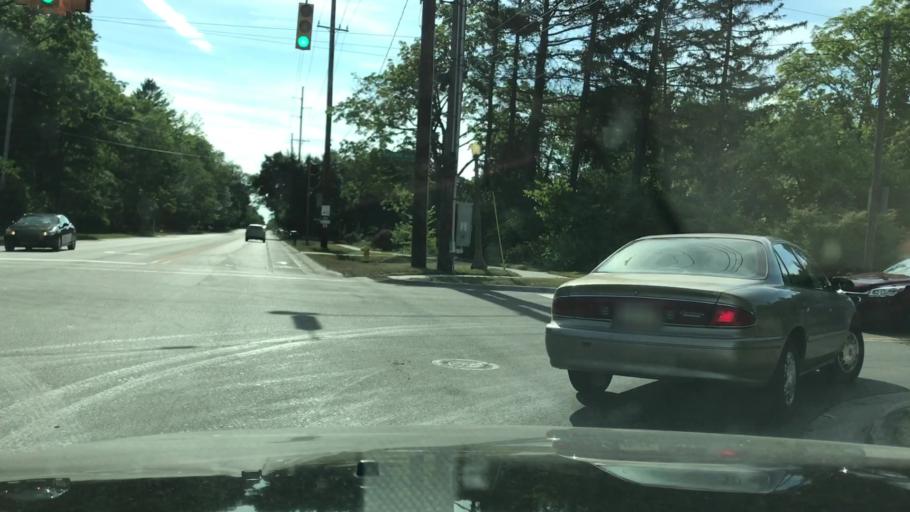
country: US
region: Michigan
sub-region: Kent County
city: East Grand Rapids
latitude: 42.9629
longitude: -85.6102
